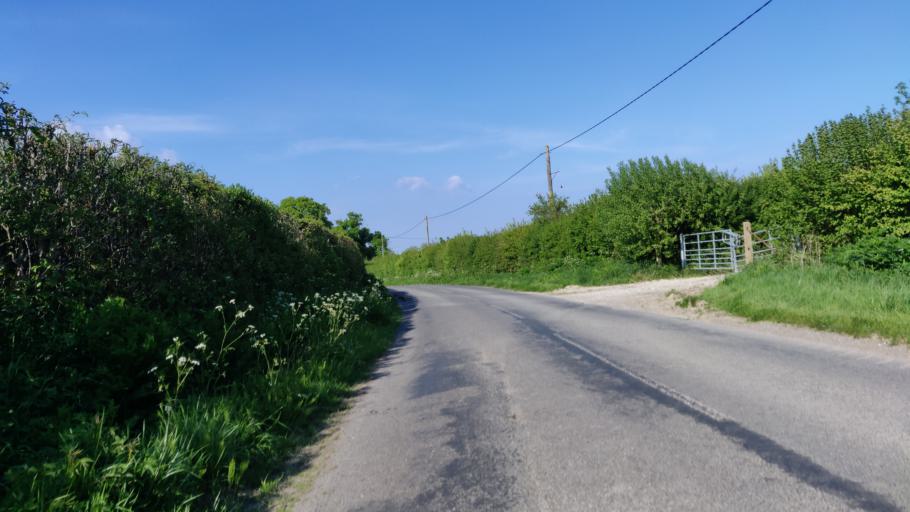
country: GB
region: England
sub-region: West Sussex
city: Southwater
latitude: 51.0373
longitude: -0.3588
